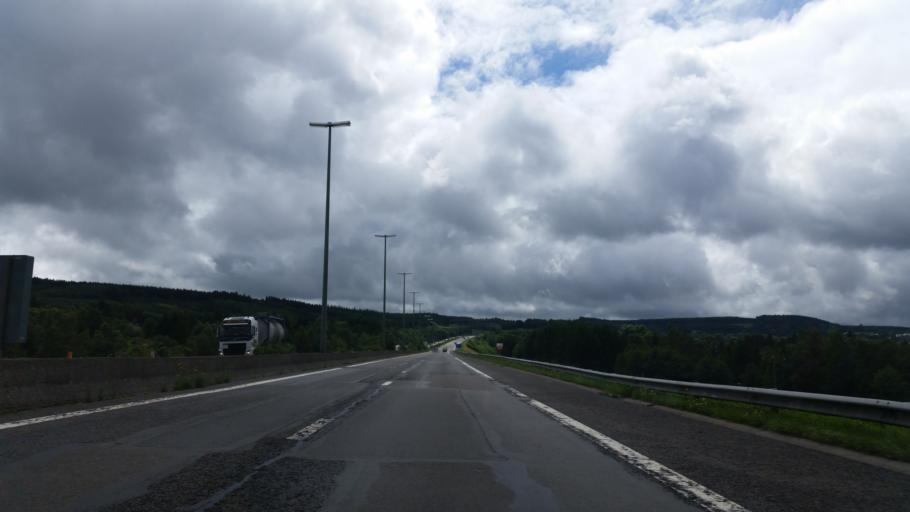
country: BE
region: Wallonia
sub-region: Province du Luxembourg
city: Manhay
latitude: 50.2965
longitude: 5.7244
